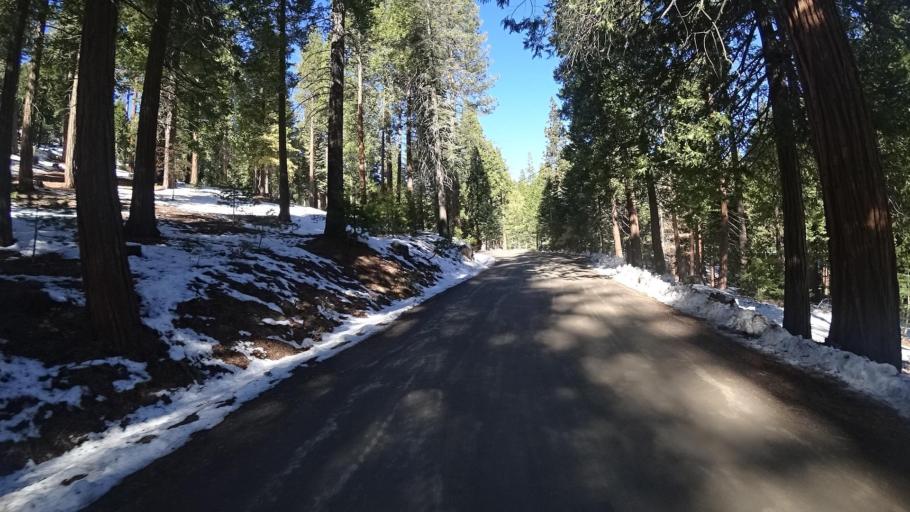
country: US
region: California
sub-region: Kern County
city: Alta Sierra
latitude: 35.7305
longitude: -118.5537
